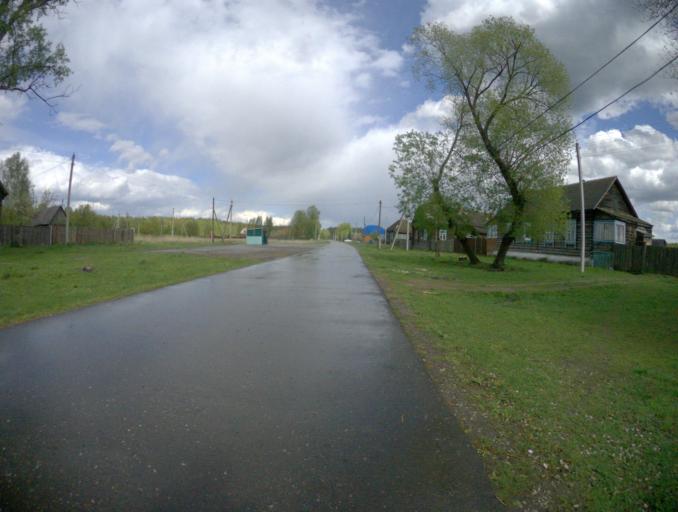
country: RU
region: Vladimir
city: Urshel'skiy
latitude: 55.5777
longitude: 40.1799
